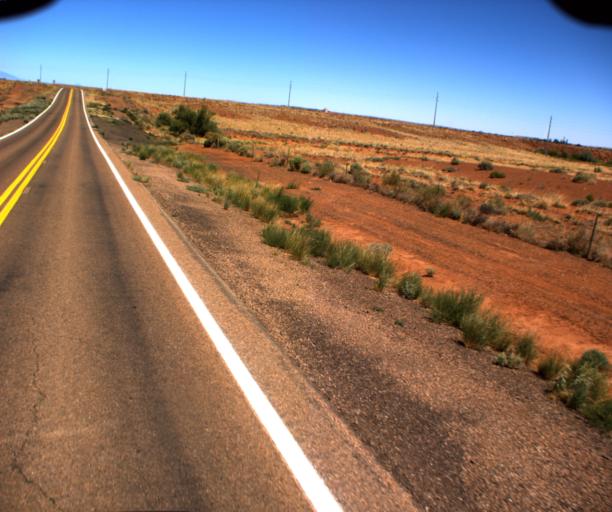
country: US
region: Arizona
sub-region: Navajo County
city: Winslow
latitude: 35.0043
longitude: -110.6894
